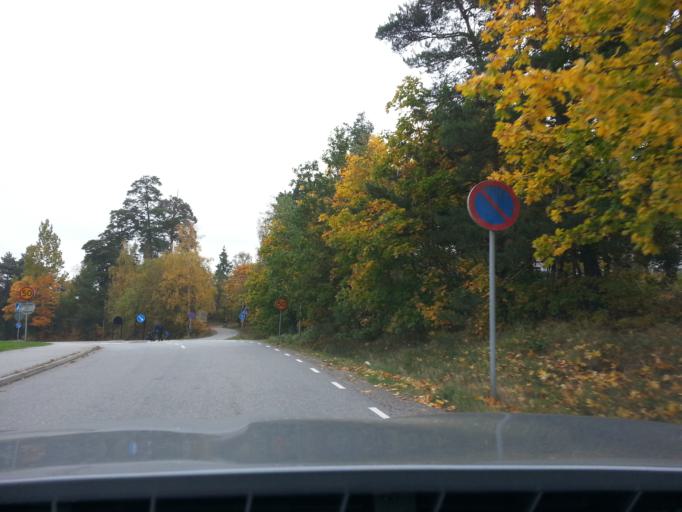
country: SE
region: Stockholm
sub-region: Vaxholms Kommun
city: Vaxholm
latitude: 59.4018
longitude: 18.3265
